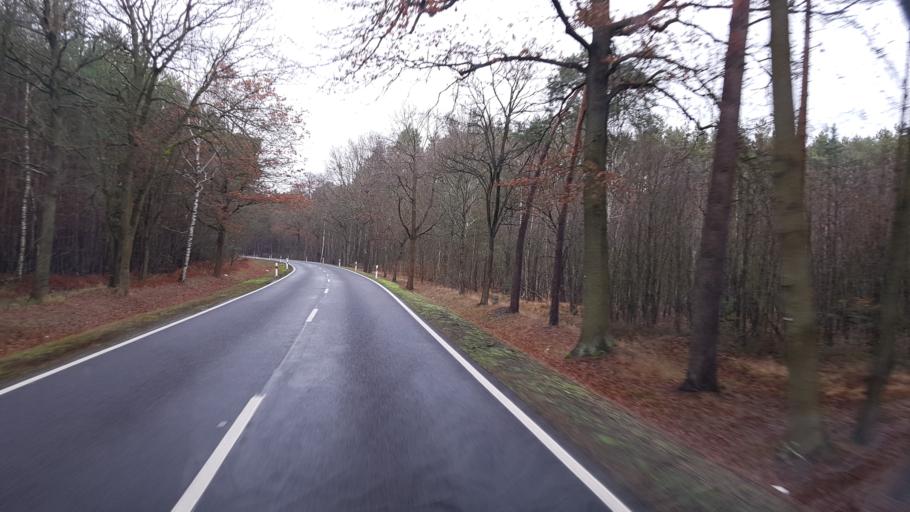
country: DE
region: Brandenburg
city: Altdobern
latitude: 51.7008
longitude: 14.0271
